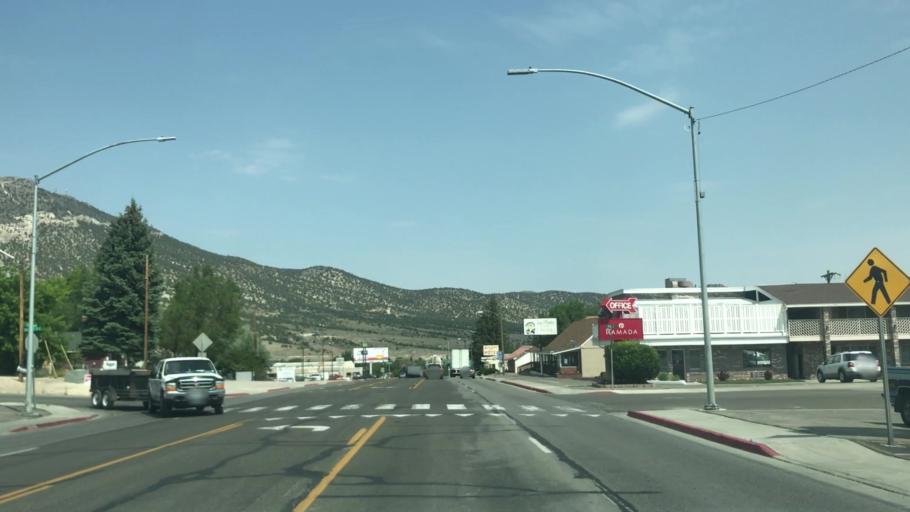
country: US
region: Nevada
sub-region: White Pine County
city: Ely
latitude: 39.2508
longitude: -114.8728
